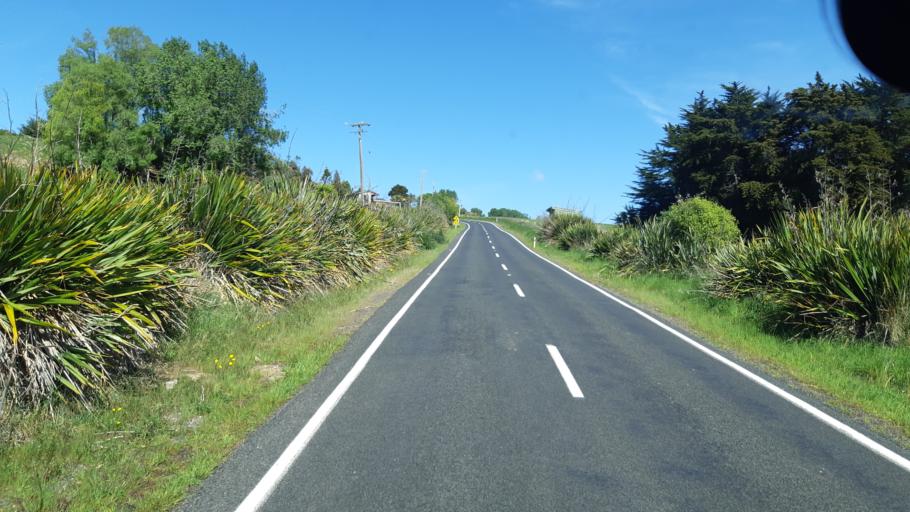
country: NZ
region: Otago
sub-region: Dunedin City
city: Portobello
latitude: -45.6551
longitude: 170.6455
